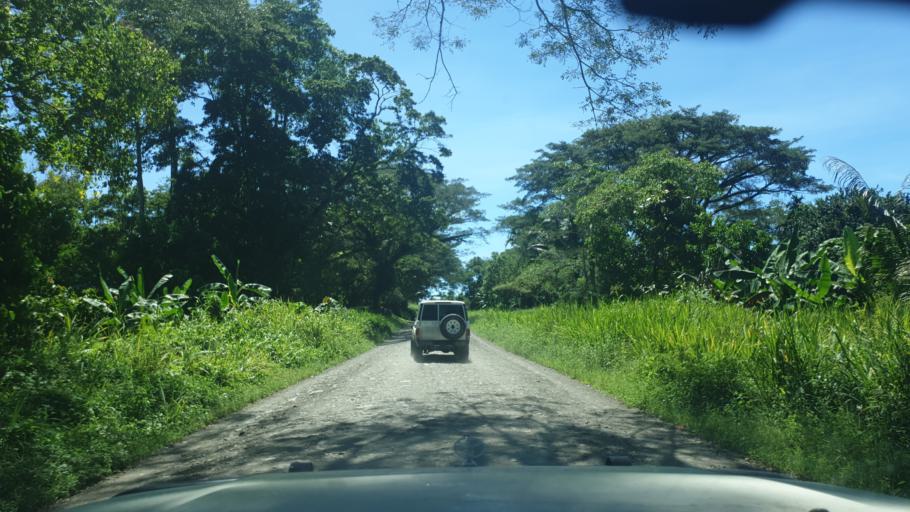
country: PG
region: Bougainville
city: Arawa
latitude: -5.8144
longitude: 155.1484
